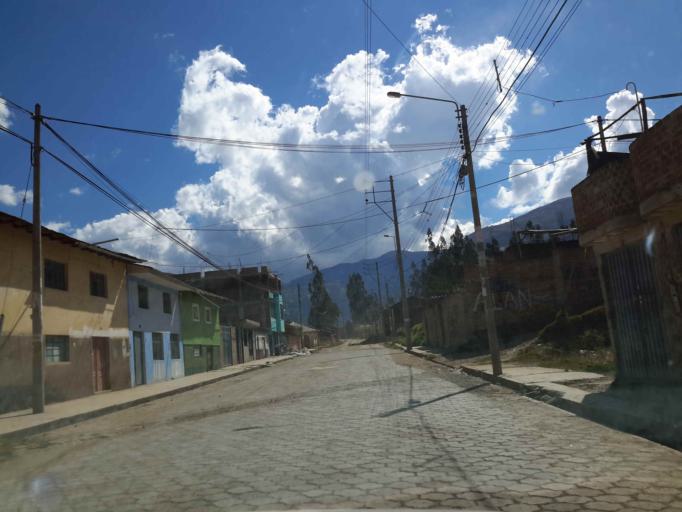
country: PE
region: Apurimac
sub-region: Provincia de Andahuaylas
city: Talavera
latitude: -13.6509
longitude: -73.4359
